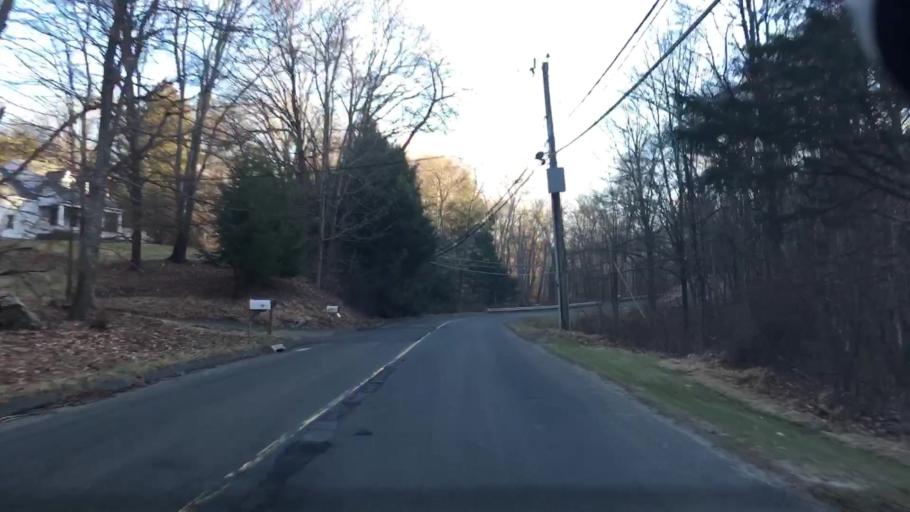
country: US
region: Connecticut
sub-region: Fairfield County
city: Newtown
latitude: 41.4557
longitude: -73.3251
